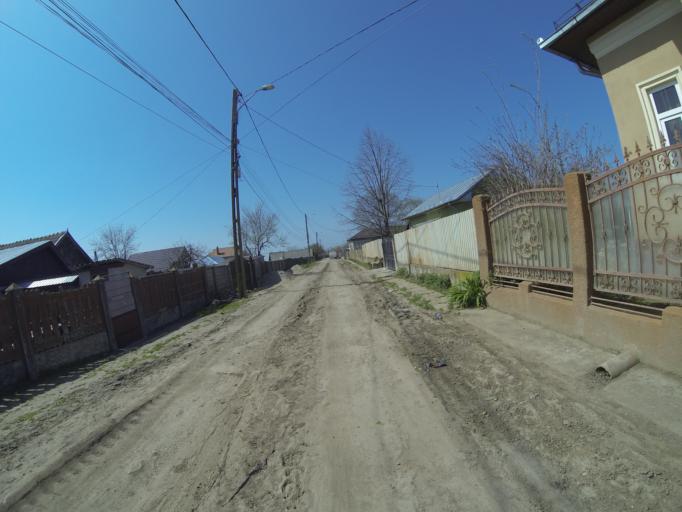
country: RO
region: Dolj
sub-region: Comuna Segarcea
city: Segarcea
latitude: 44.0992
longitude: 23.7336
